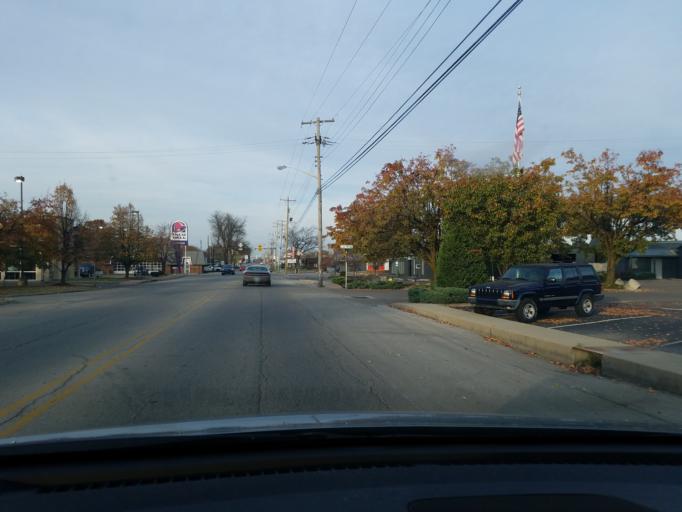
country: US
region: Indiana
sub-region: Floyd County
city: New Albany
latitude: 38.3120
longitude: -85.8065
